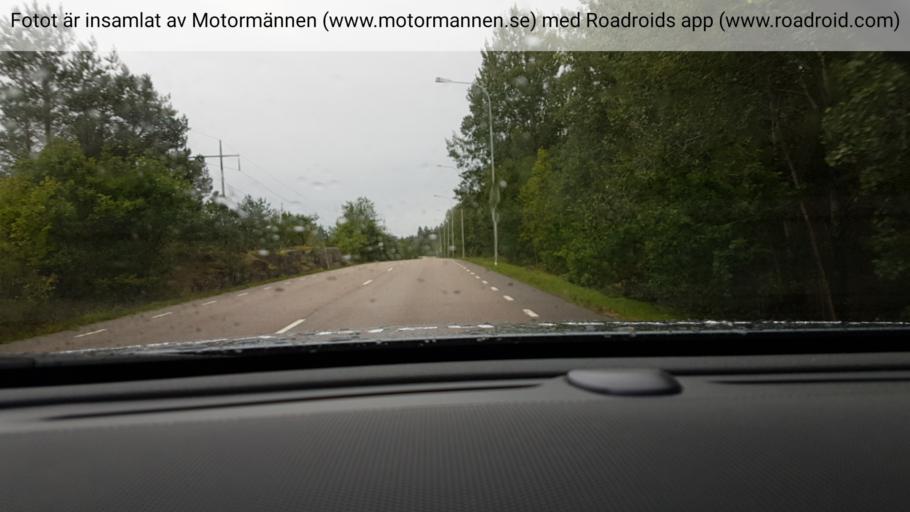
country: SE
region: Vaestra Goetaland
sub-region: Vanersborgs Kommun
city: Vanersborg
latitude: 58.3527
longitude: 12.3438
